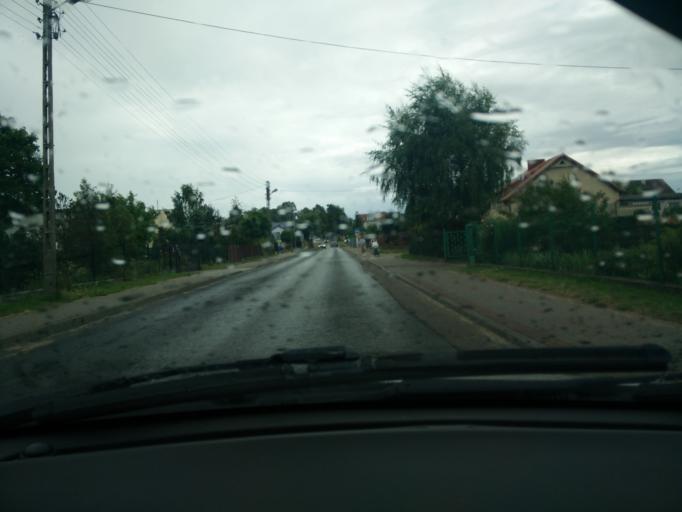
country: PL
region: Pomeranian Voivodeship
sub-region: Powiat pucki
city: Mosty
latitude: 54.6099
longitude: 18.4959
